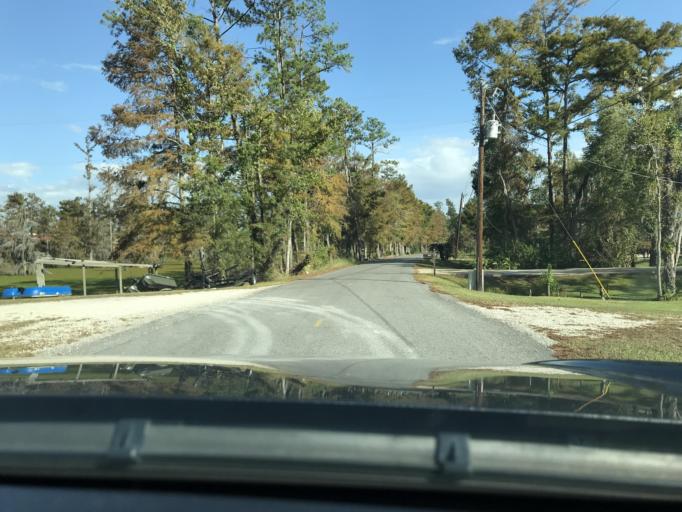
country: US
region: Louisiana
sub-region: Calcasieu Parish
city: Westlake
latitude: 30.3158
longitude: -93.2884
